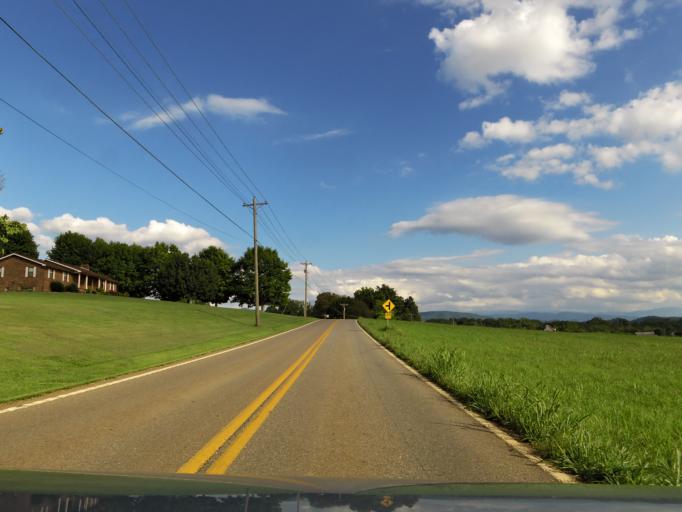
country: US
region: Tennessee
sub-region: Loudon County
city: Greenback
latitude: 35.6434
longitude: -84.1018
